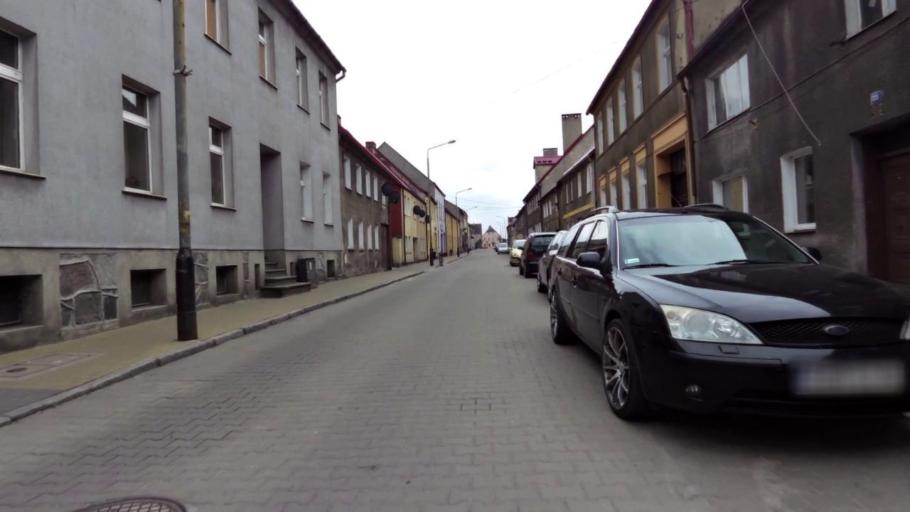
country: PL
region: West Pomeranian Voivodeship
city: Trzcinsko Zdroj
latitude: 52.9674
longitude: 14.6064
